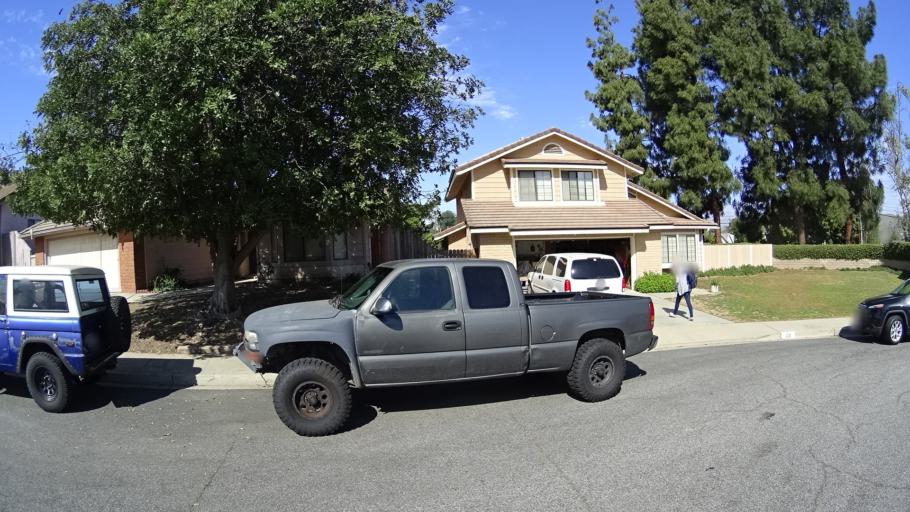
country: US
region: California
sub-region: Ventura County
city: Casa Conejo
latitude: 34.1792
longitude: -118.9318
